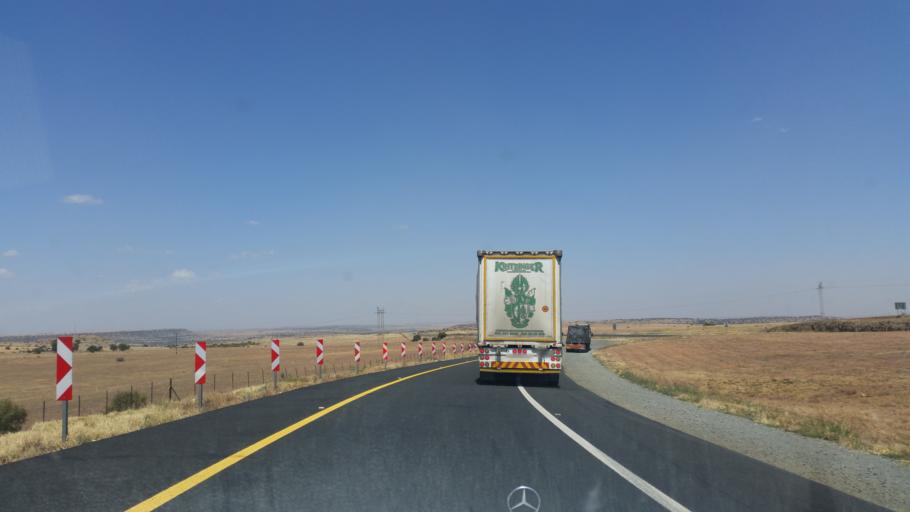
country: ZA
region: Orange Free State
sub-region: Lejweleputswa District Municipality
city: Winburg
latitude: -28.5000
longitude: 26.9978
